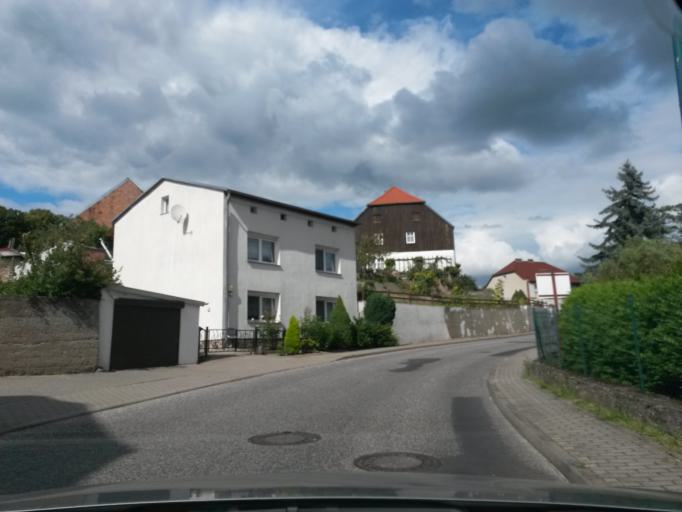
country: DE
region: Brandenburg
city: Liepe
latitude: 52.8618
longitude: 13.9690
